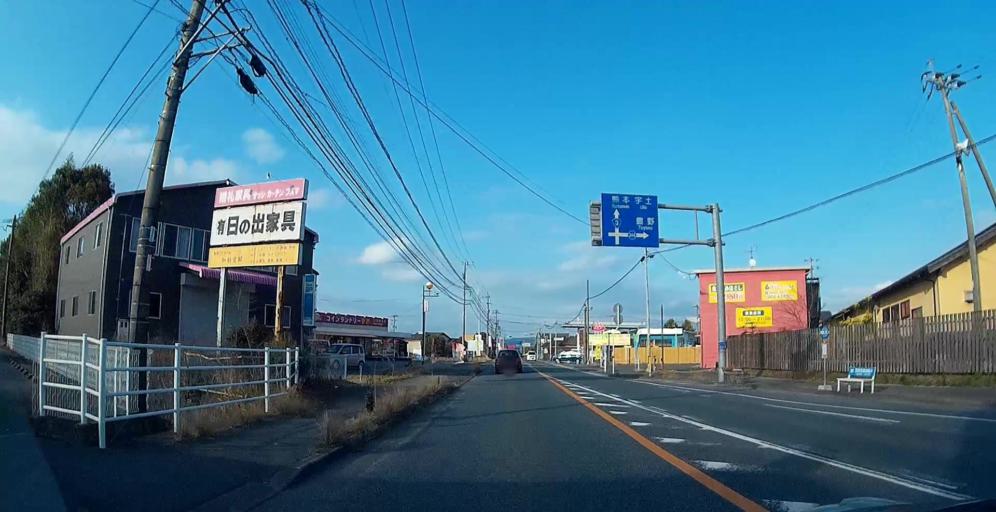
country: JP
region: Kumamoto
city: Matsubase
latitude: 32.5994
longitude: 130.7023
